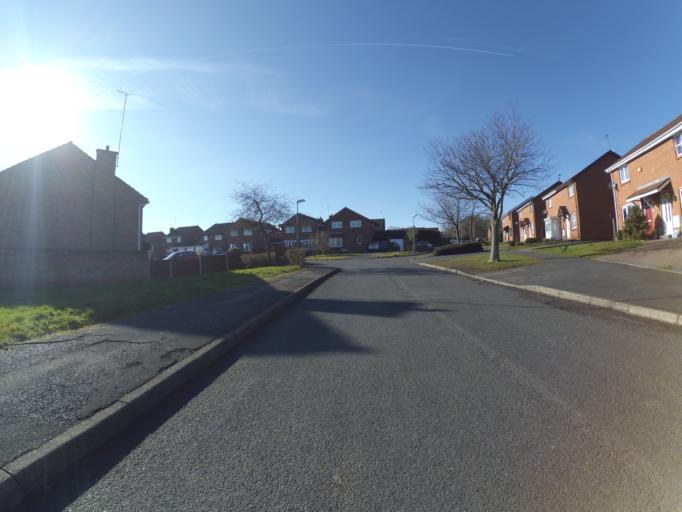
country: GB
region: England
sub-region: Warwickshire
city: Rugby
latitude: 52.3903
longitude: -1.2403
